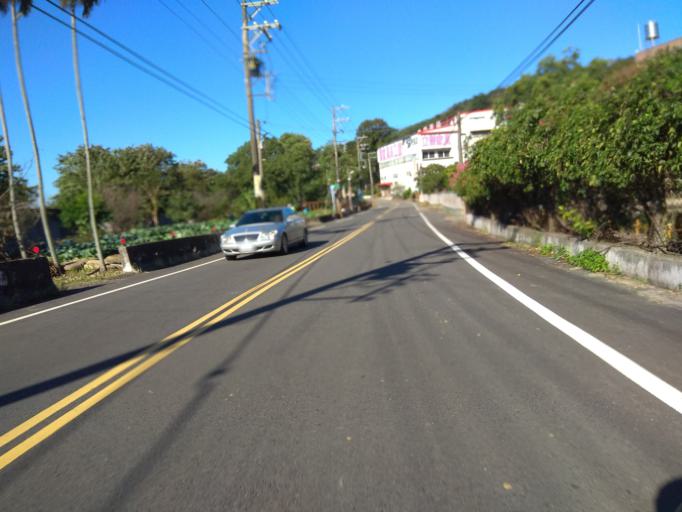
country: TW
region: Taiwan
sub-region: Hsinchu
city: Zhubei
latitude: 24.8449
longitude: 121.1369
